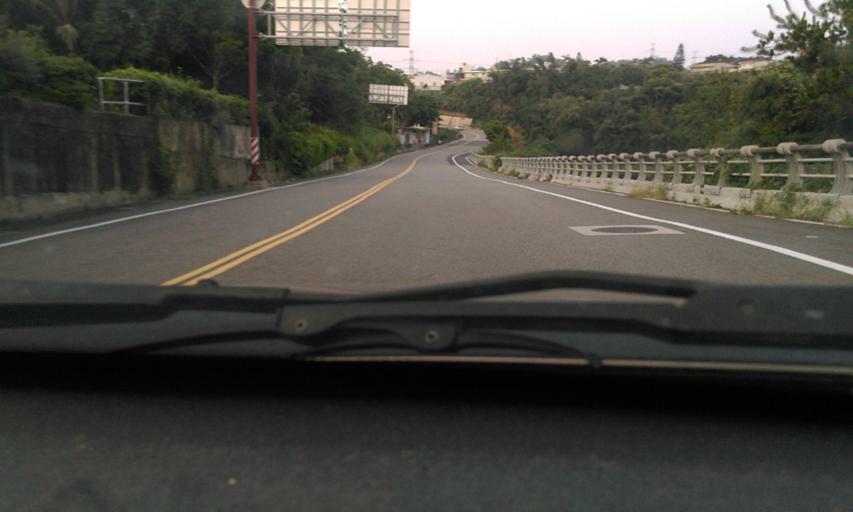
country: TW
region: Taiwan
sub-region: Hsinchu
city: Hsinchu
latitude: 24.6846
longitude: 120.9855
